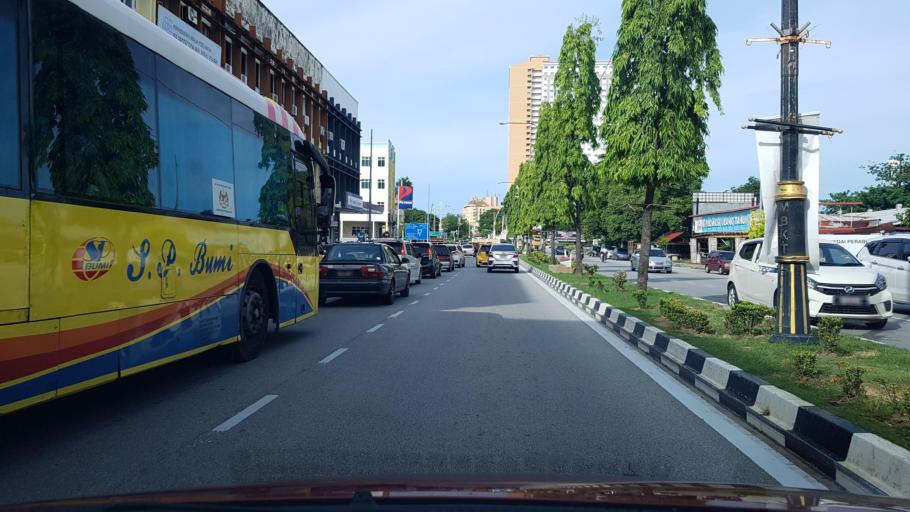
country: MY
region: Terengganu
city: Kuala Terengganu
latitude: 5.3284
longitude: 103.1444
